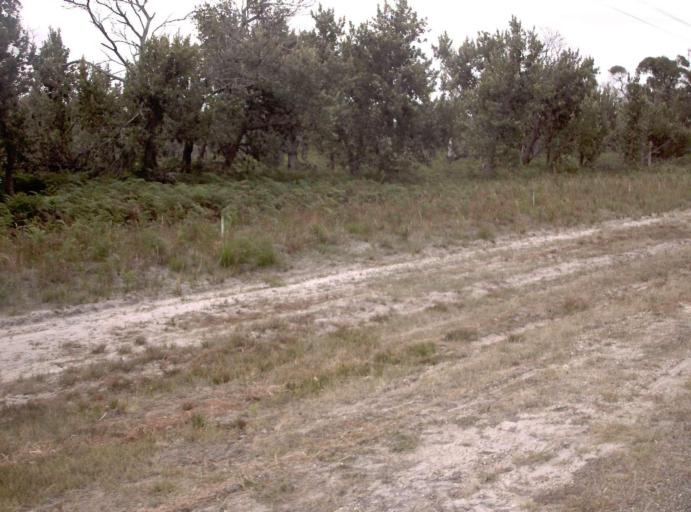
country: AU
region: Victoria
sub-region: East Gippsland
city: Bairnsdale
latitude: -38.0692
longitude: 147.5508
